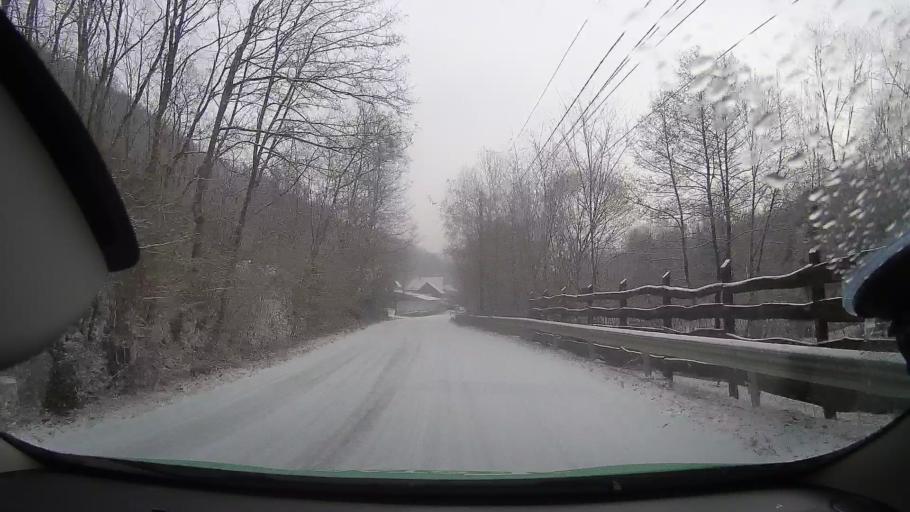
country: RO
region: Alba
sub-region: Comuna Livezile
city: Livezile
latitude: 46.3665
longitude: 23.5935
